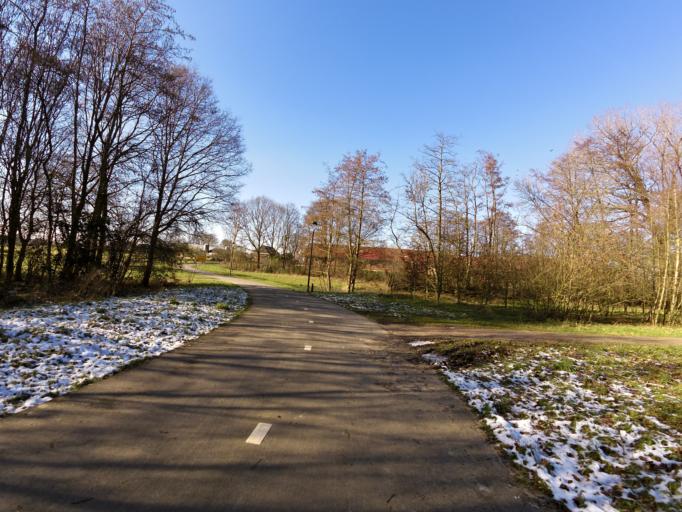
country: NL
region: Gelderland
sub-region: Gemeente Doetinchem
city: Doetinchem
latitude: 51.9521
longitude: 6.2834
